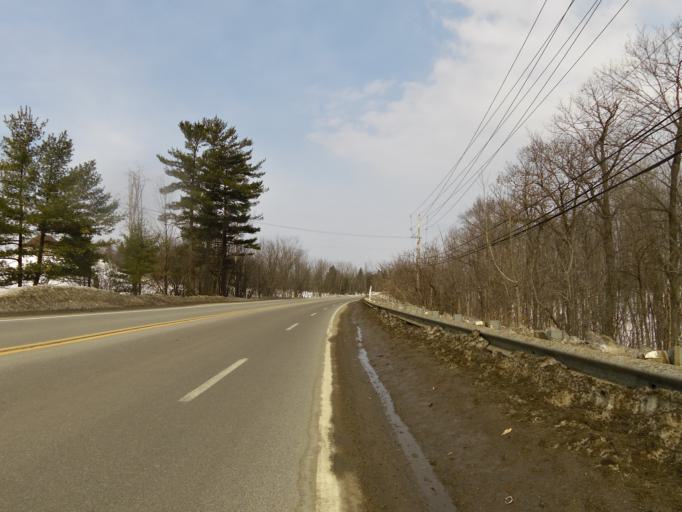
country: CA
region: Quebec
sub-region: Outaouais
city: Gatineau
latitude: 45.4854
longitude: -75.7564
